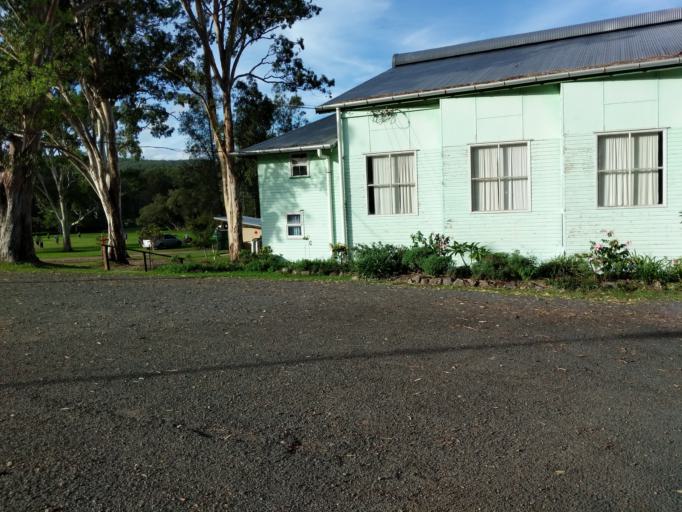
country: AU
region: New South Wales
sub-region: Port Stephens Shire
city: Port Stephens
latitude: -32.6686
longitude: 152.0047
